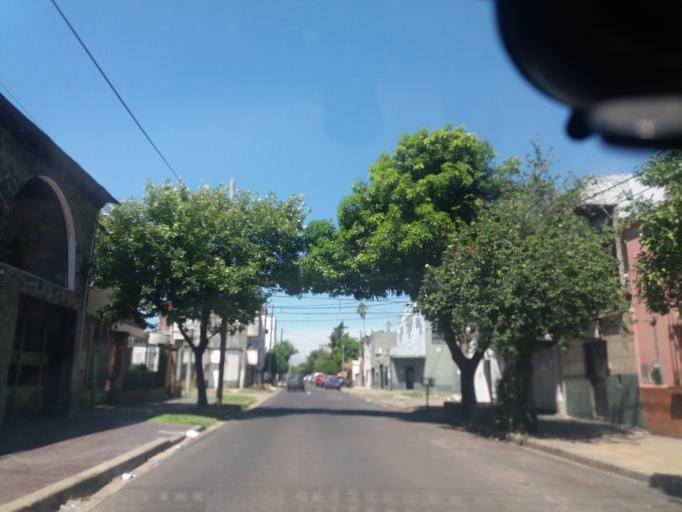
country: AR
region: Corrientes
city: Corrientes
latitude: -27.4792
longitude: -58.8449
